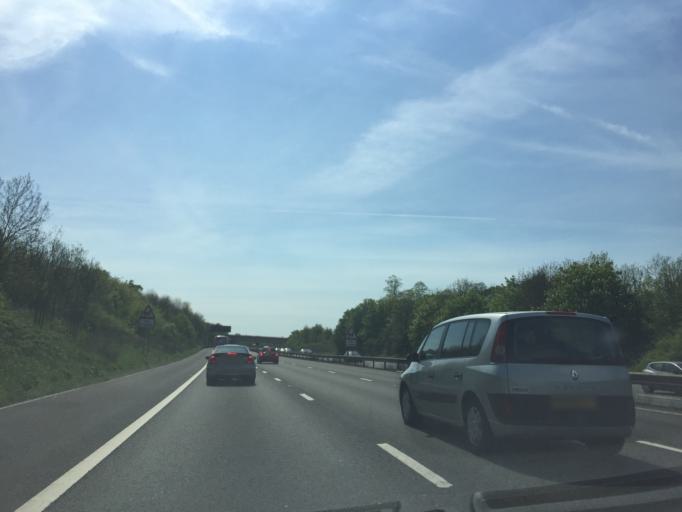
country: GB
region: England
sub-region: Essex
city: Chigwell
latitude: 51.6230
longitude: 0.0640
